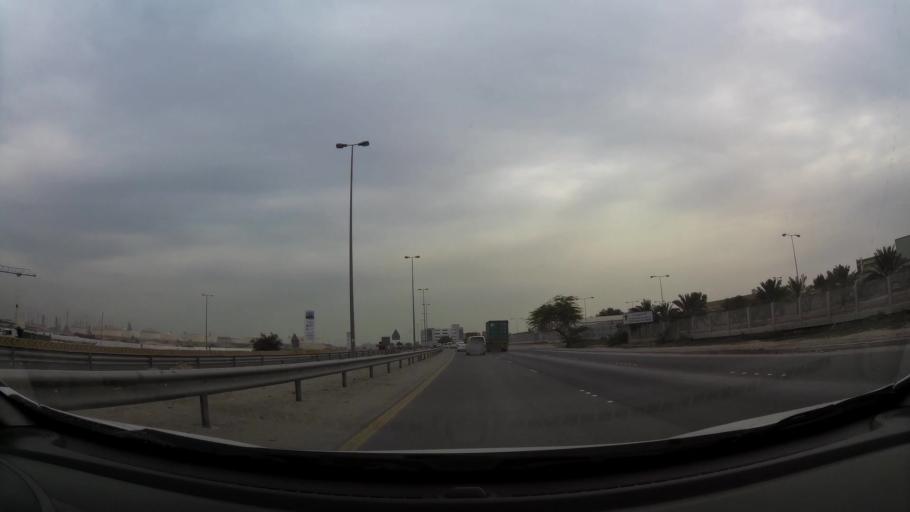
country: BH
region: Northern
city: Ar Rifa'
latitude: 26.1215
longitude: 50.5919
